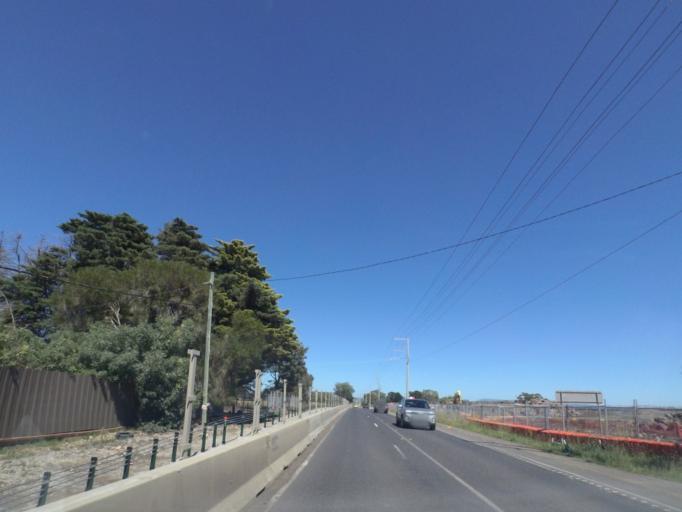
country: AU
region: Victoria
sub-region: Hume
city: Craigieburn
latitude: -37.5437
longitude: 144.9794
